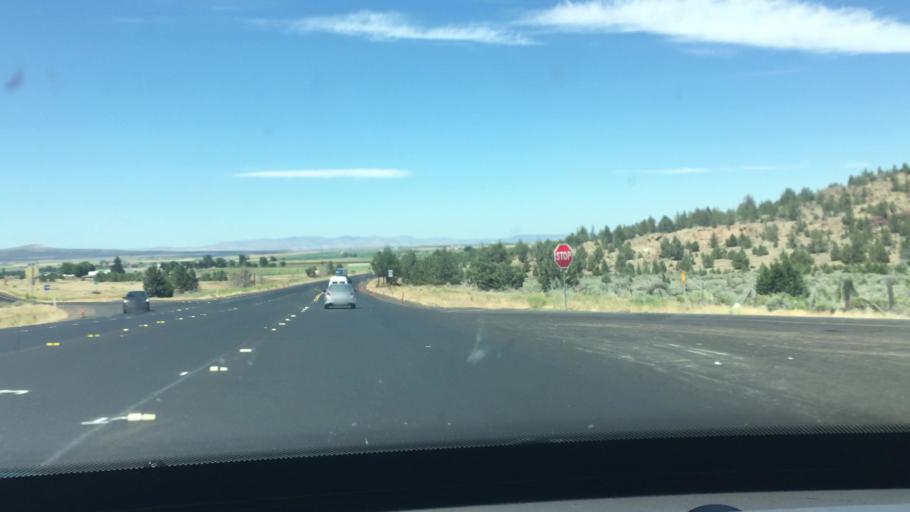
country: US
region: Oregon
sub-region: Jefferson County
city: Culver
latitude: 44.4906
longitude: -121.1932
